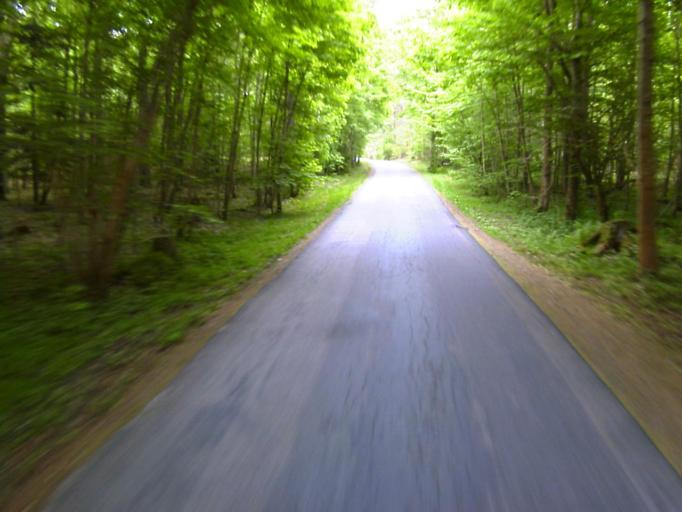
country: SE
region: Skane
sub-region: Kristianstads Kommun
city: Ahus
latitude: 55.9219
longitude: 14.3153
